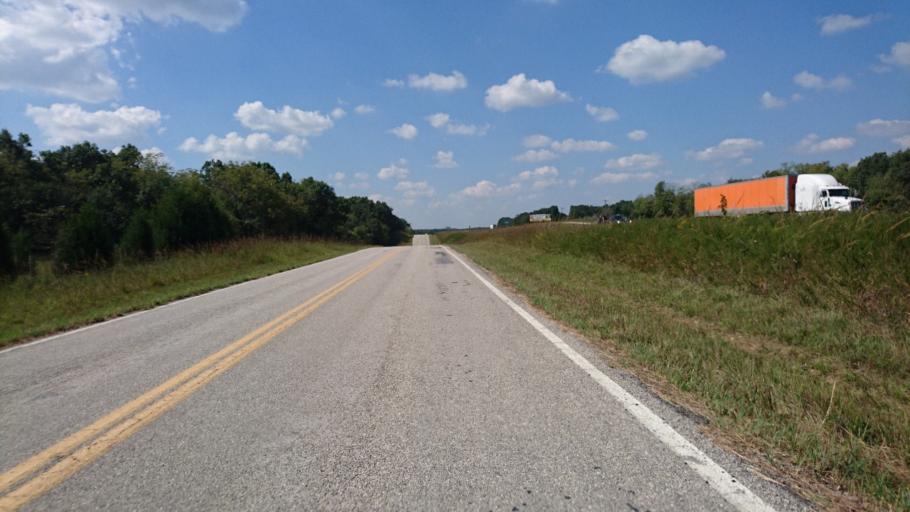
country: US
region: Missouri
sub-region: Pulaski County
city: Richland
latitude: 37.7558
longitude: -92.4800
